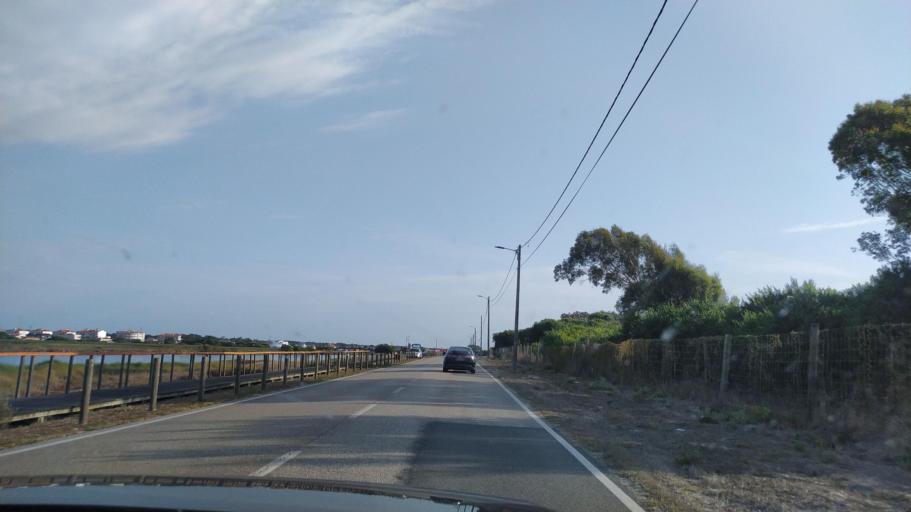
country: PT
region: Aveiro
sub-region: Ilhavo
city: Gafanha da Encarnacao
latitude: 40.5668
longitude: -8.7570
